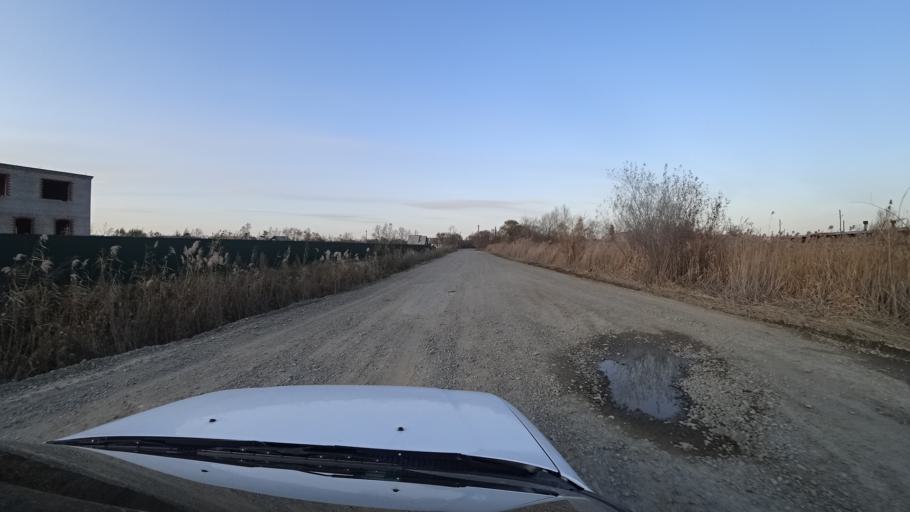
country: RU
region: Primorskiy
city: Dal'nerechensk
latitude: 45.9388
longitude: 133.8206
